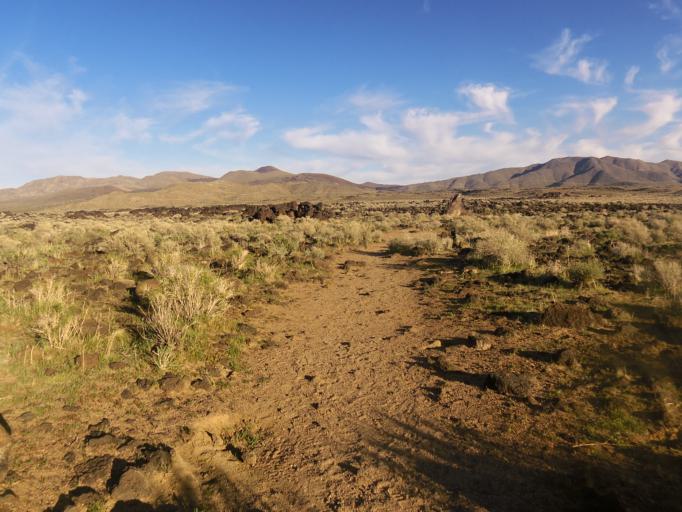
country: US
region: California
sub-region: Kern County
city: Inyokern
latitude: 35.9711
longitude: -117.9088
